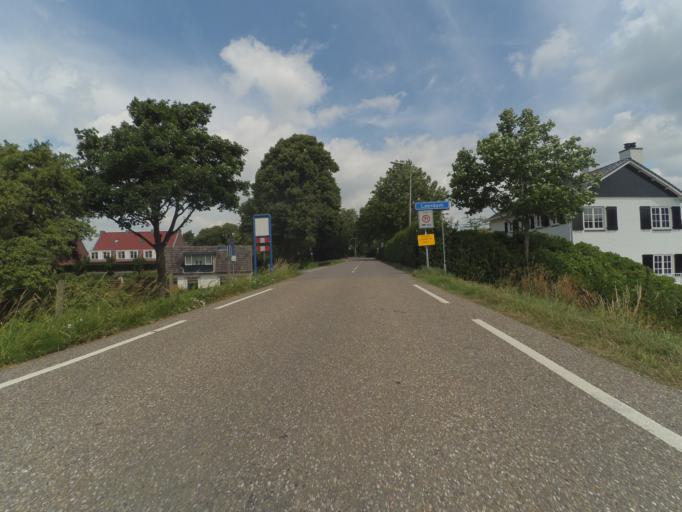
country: NL
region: South Holland
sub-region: Gemeente Leerdam
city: Leerdam
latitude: 51.8804
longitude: 5.0846
